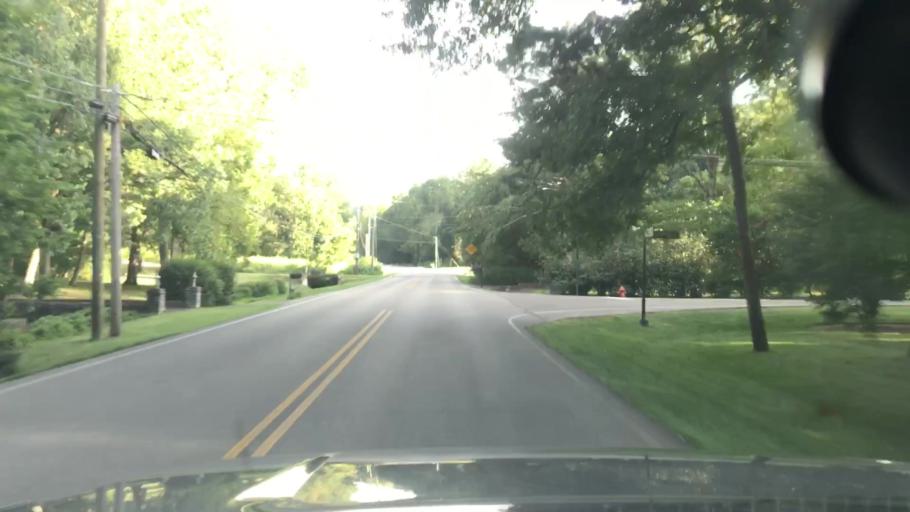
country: US
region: Tennessee
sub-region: Davidson County
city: Forest Hills
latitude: 36.0559
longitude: -86.8443
